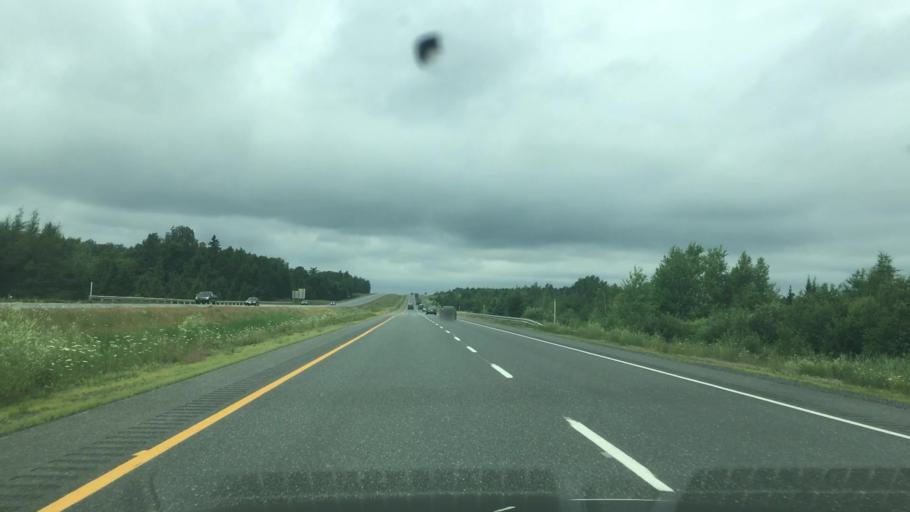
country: CA
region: Nova Scotia
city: Truro
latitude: 45.3871
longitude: -63.3820
